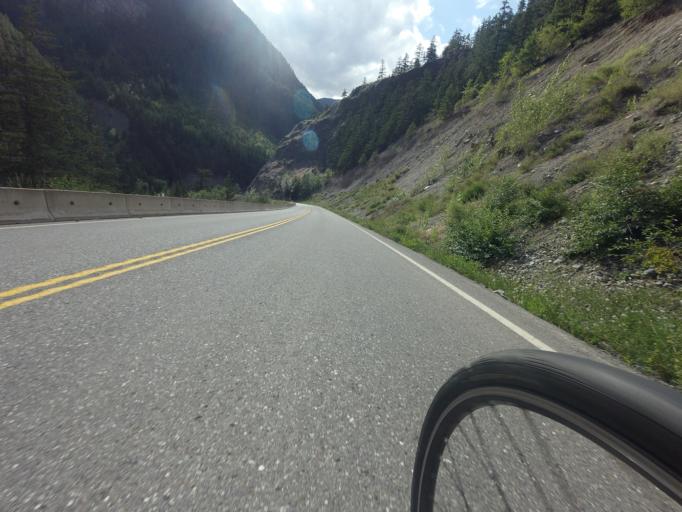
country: CA
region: British Columbia
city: Lillooet
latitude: 50.6428
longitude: -122.0474
